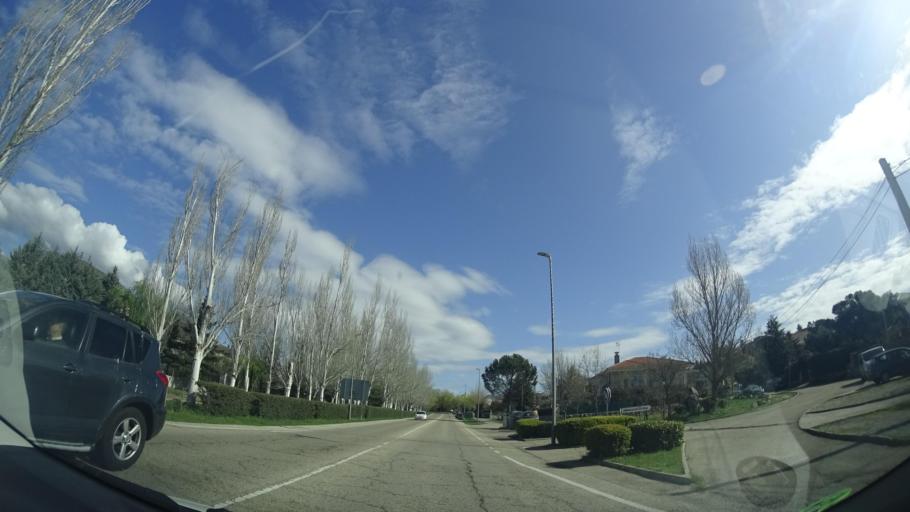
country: ES
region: Madrid
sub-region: Provincia de Madrid
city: Miraflores de la Sierra
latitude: 40.7501
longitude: -3.7827
